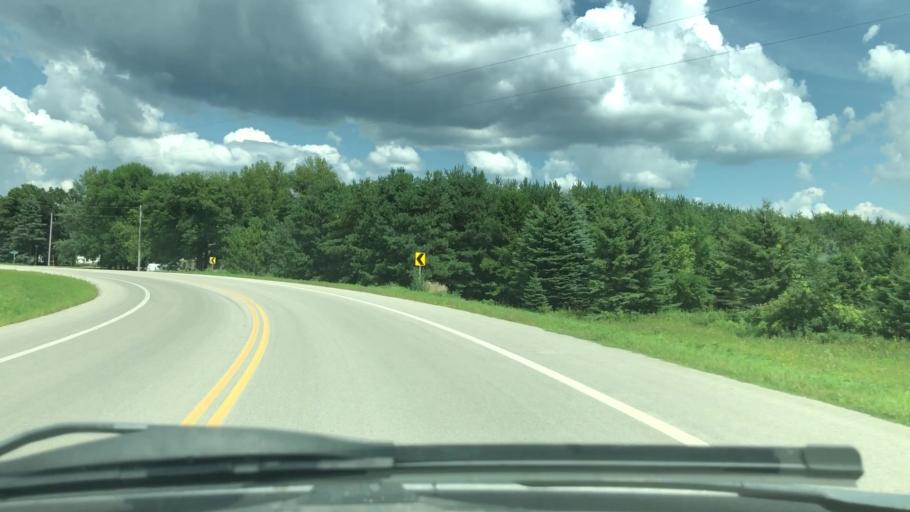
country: US
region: Minnesota
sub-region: Olmsted County
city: Rochester
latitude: 43.9501
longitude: -92.5187
